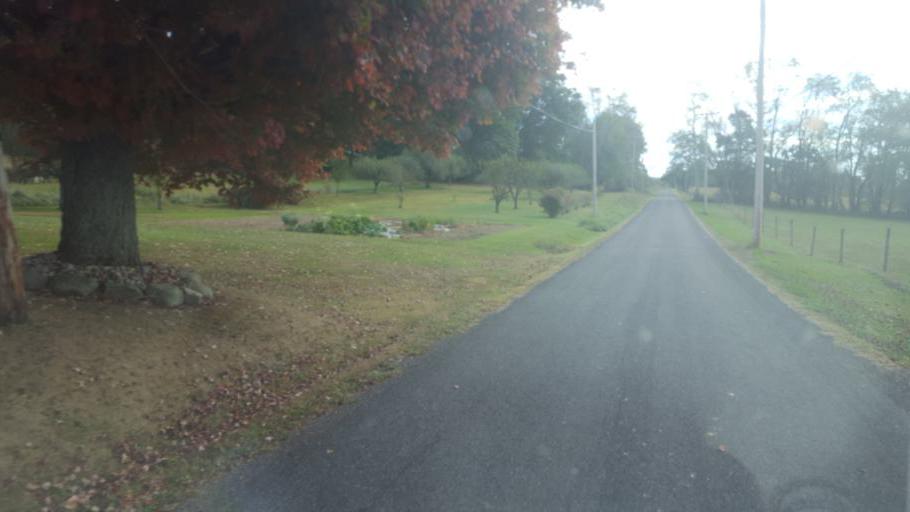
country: US
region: Pennsylvania
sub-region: Mercer County
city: Mercer
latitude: 41.3296
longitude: -80.2650
